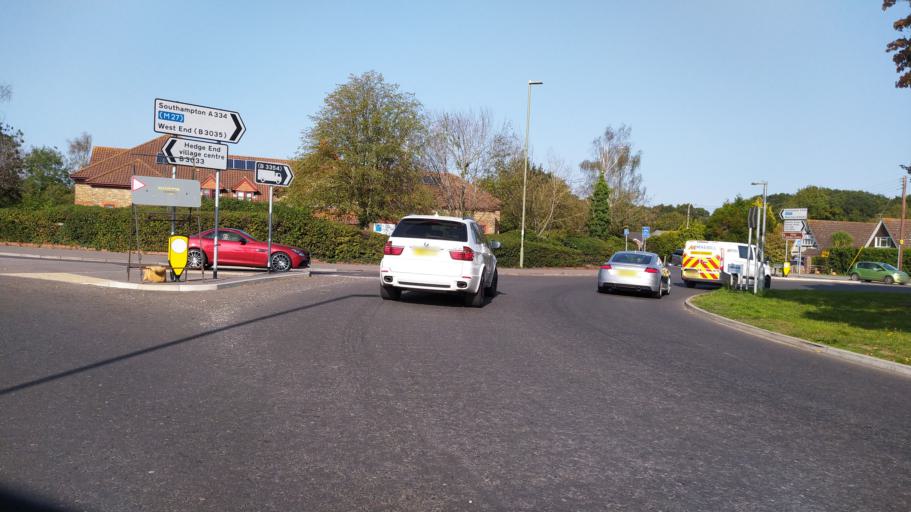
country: GB
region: England
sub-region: Hampshire
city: Hedge End
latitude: 50.9161
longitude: -1.2913
